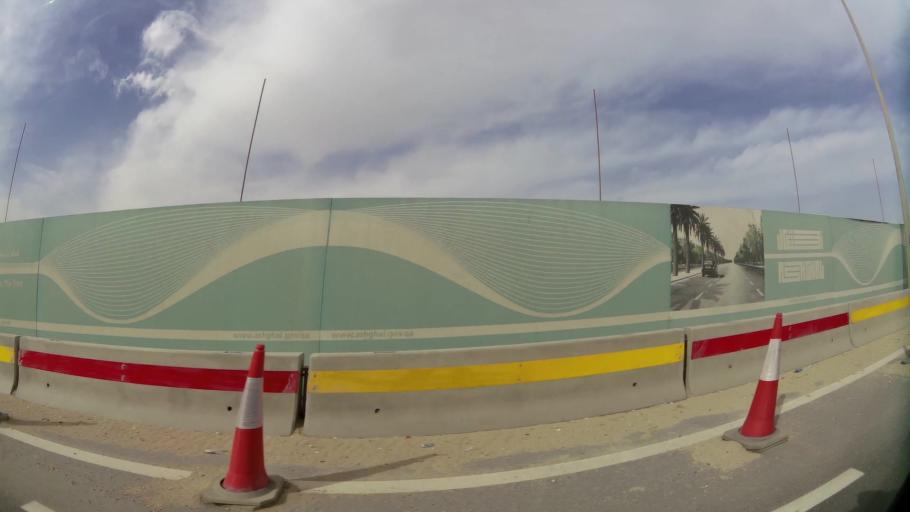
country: QA
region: Baladiyat ar Rayyan
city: Ar Rayyan
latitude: 25.3092
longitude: 51.4005
